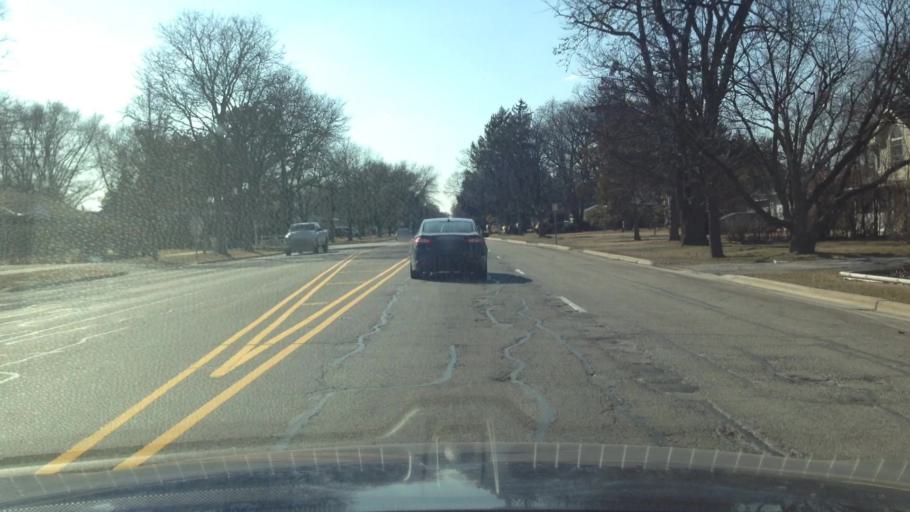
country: US
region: Illinois
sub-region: Cook County
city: Glenview
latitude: 42.0657
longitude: -87.8174
